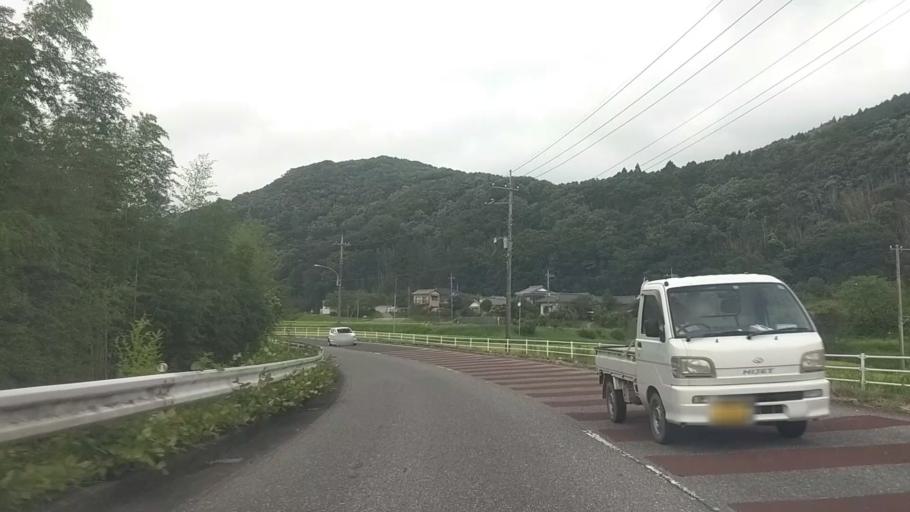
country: JP
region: Chiba
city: Kimitsu
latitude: 35.2622
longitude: 140.0044
